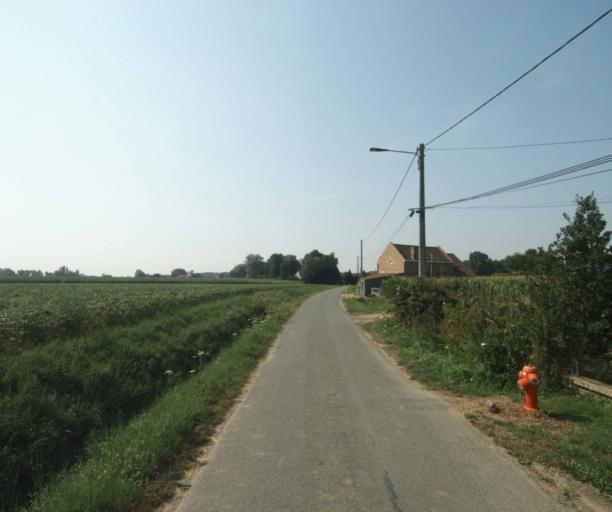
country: FR
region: Nord-Pas-de-Calais
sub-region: Departement du Nord
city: Quesnoy-sur-Deule
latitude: 50.7039
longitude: 2.9990
